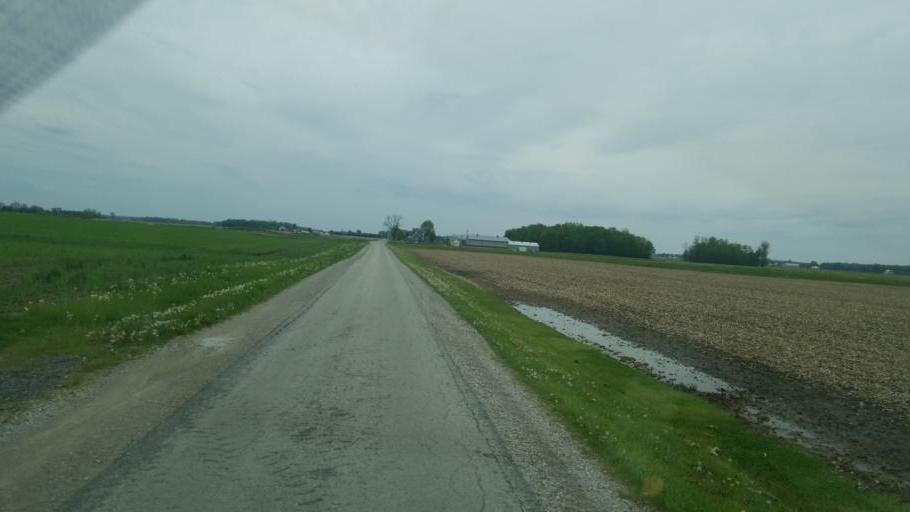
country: US
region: Ohio
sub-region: Huron County
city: Willard
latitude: 41.0251
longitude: -82.7991
